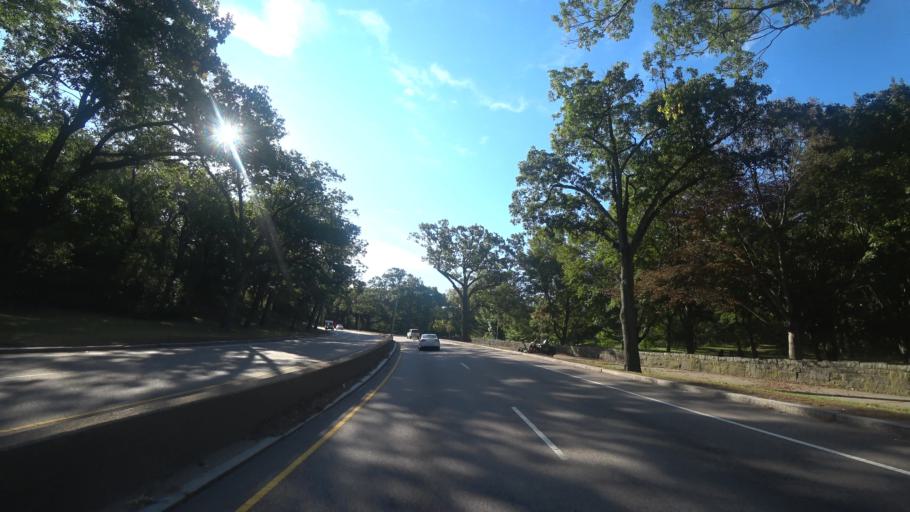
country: US
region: Massachusetts
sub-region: Suffolk County
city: Jamaica Plain
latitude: 42.3044
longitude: -71.1199
